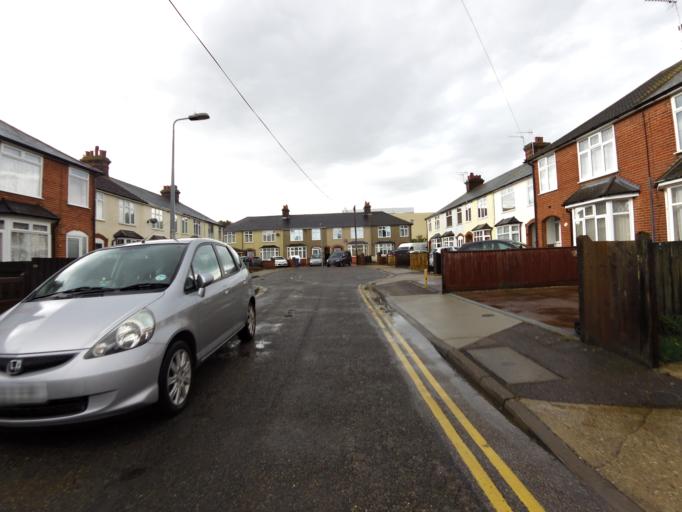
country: GB
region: England
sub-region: Suffolk
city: Kesgrave
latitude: 52.0547
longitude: 1.2003
